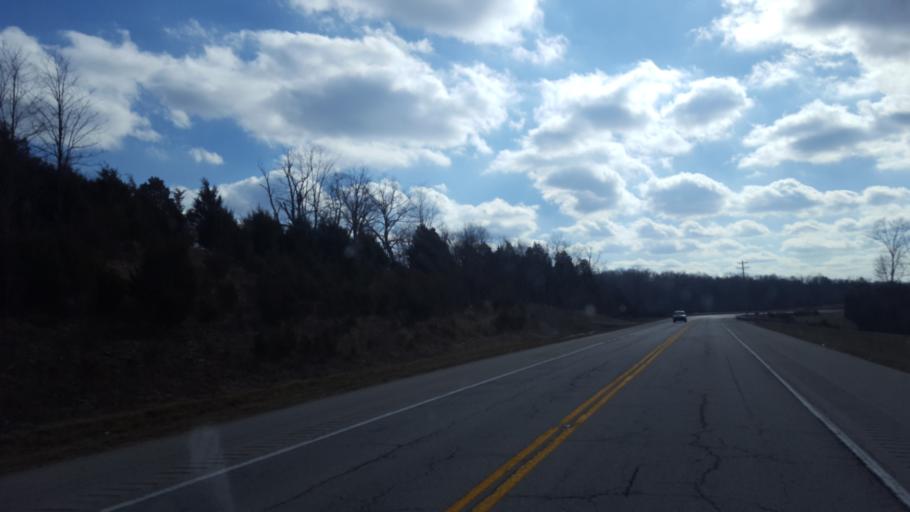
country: US
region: Kentucky
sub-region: Owen County
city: Owenton
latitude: 38.3828
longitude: -84.8555
